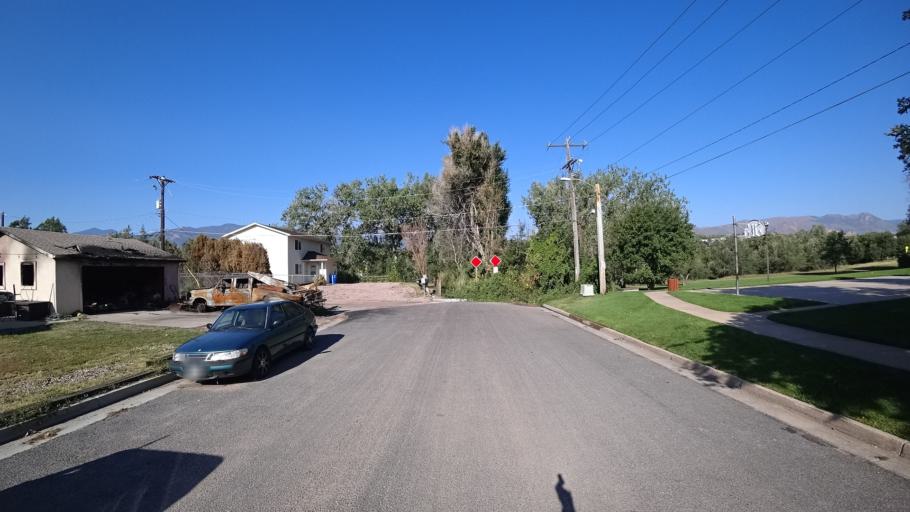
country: US
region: Colorado
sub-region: El Paso County
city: Colorado Springs
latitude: 38.8712
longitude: -104.8300
